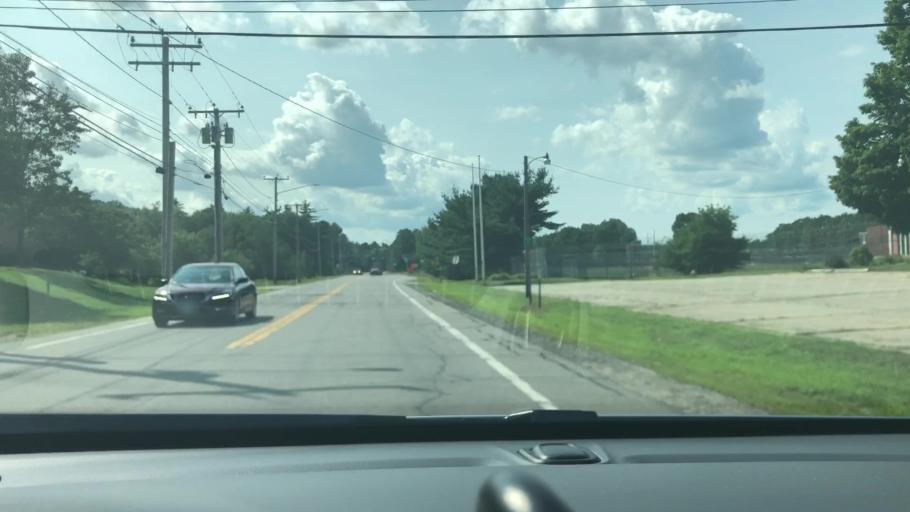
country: US
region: New Hampshire
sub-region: Hillsborough County
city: Pinardville
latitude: 43.0095
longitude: -71.5386
